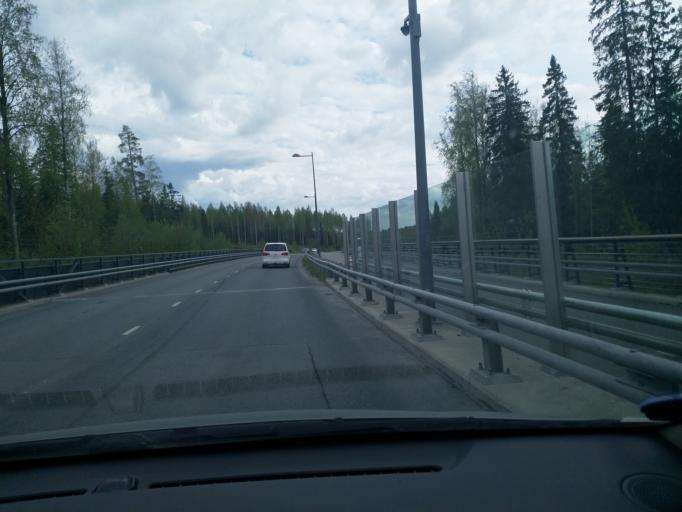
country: FI
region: Pirkanmaa
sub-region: Tampere
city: Tampere
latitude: 61.4486
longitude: 23.8059
